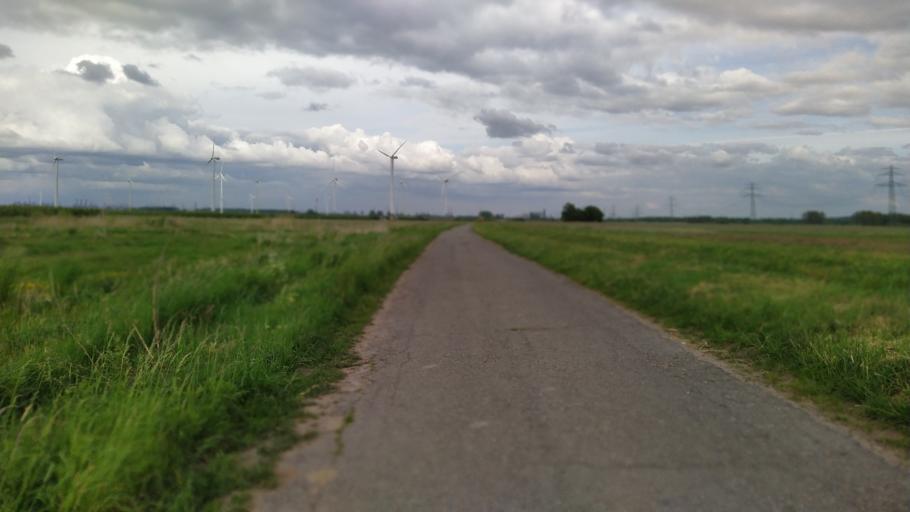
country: DE
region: Lower Saxony
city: Neu Wulmstorf
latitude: 53.4960
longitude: 9.8304
